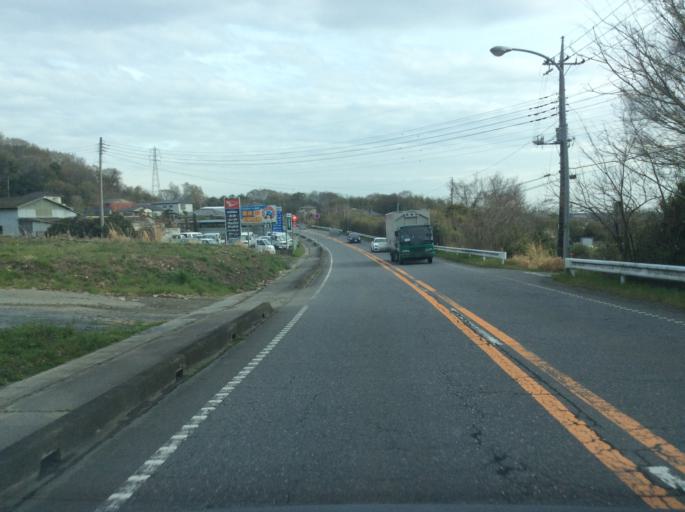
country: JP
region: Ibaraki
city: Tsukuba
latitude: 36.1605
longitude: 140.1073
